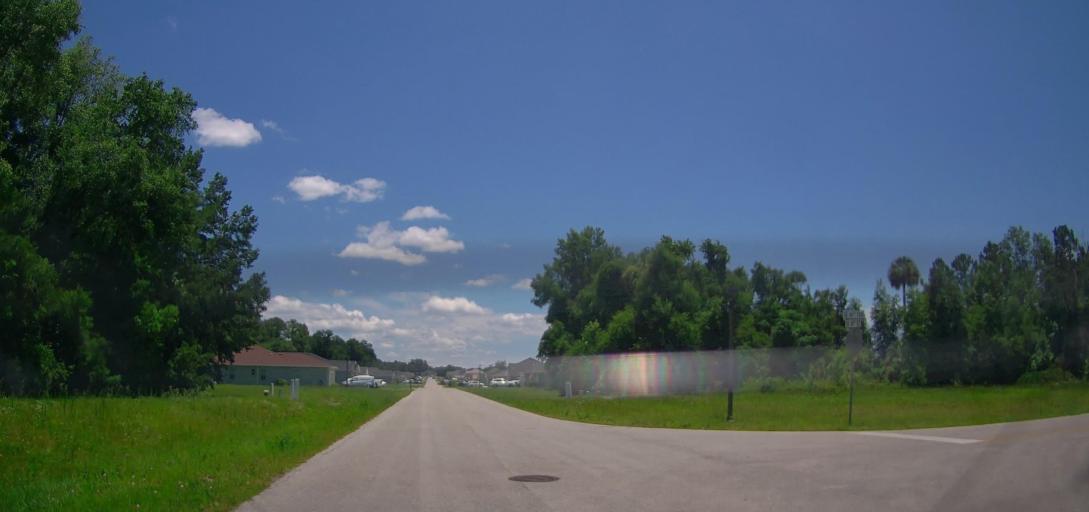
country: US
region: Florida
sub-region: Marion County
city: Belleview
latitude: 29.0930
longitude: -82.0702
